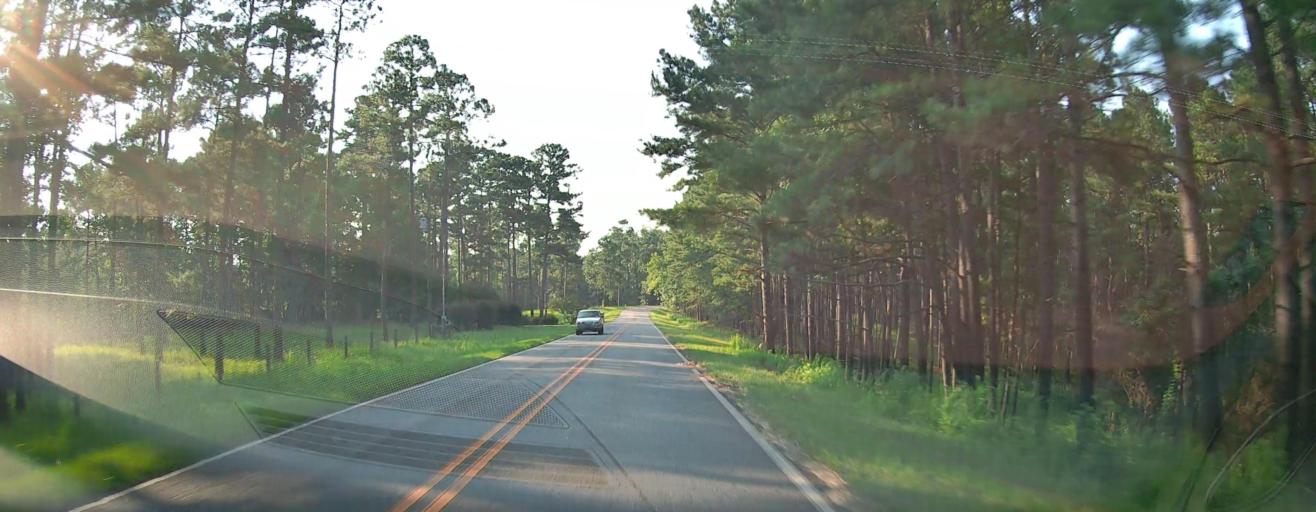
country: US
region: Georgia
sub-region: Bibb County
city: West Point
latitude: 32.8782
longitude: -83.8318
